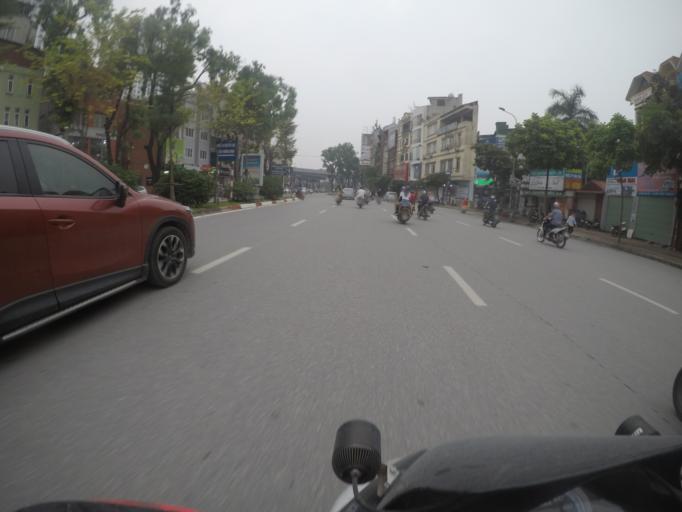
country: VN
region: Ha Noi
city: Dong Da
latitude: 21.0042
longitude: 105.8183
